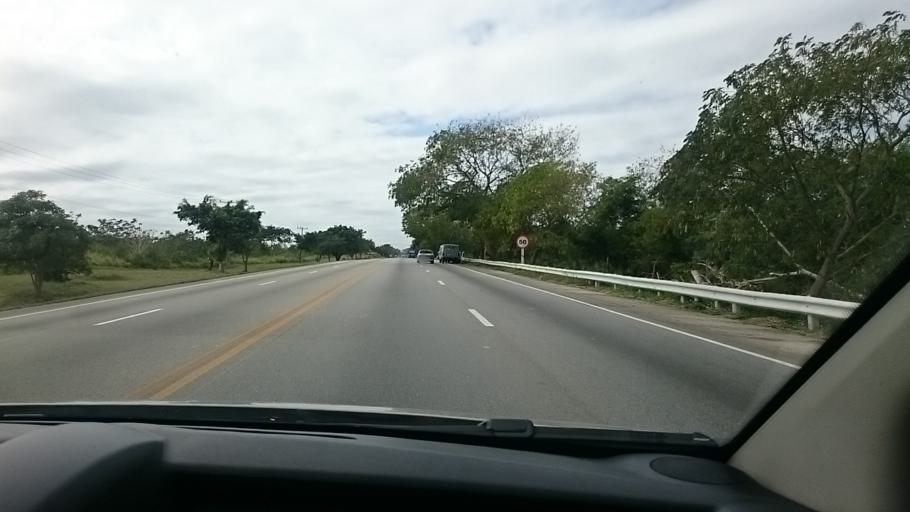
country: CU
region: La Habana
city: Alamar
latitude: 23.1642
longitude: -82.2611
